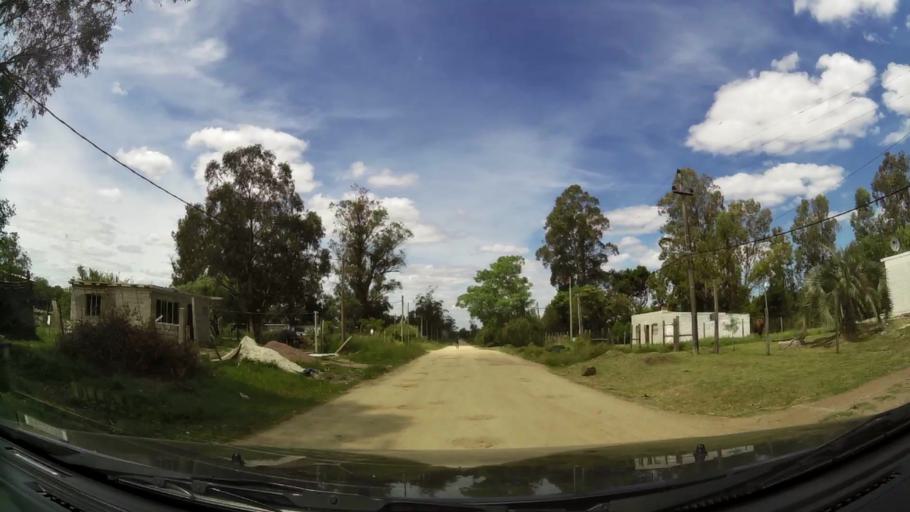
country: UY
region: Canelones
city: Empalme Olmos
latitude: -34.7769
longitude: -55.8871
